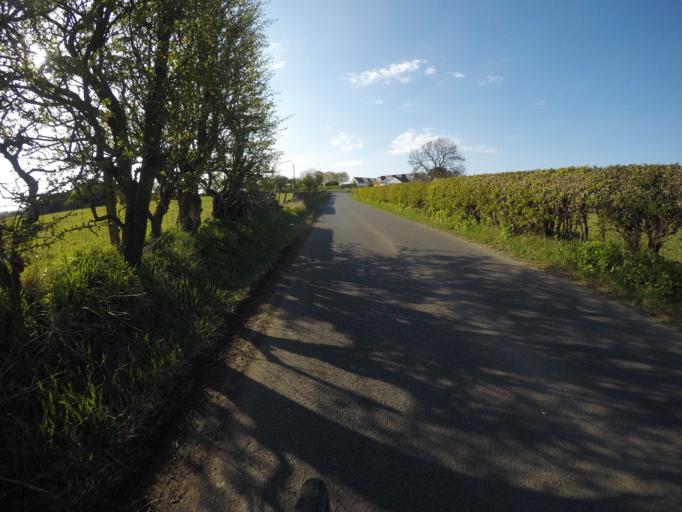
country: GB
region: Scotland
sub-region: North Ayrshire
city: Stevenston
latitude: 55.6498
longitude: -4.7320
